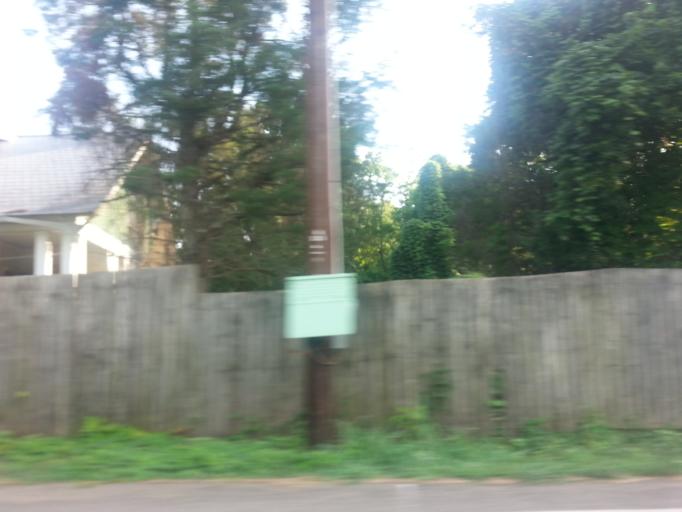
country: US
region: Tennessee
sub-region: Loudon County
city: Greenback
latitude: 35.7575
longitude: -84.1322
